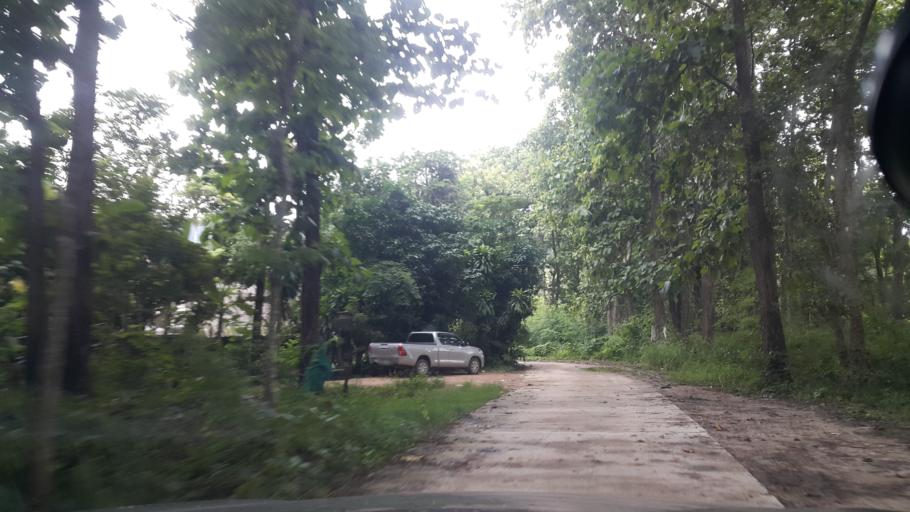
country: TH
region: Chiang Mai
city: San Sai
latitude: 18.9840
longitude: 99.1214
